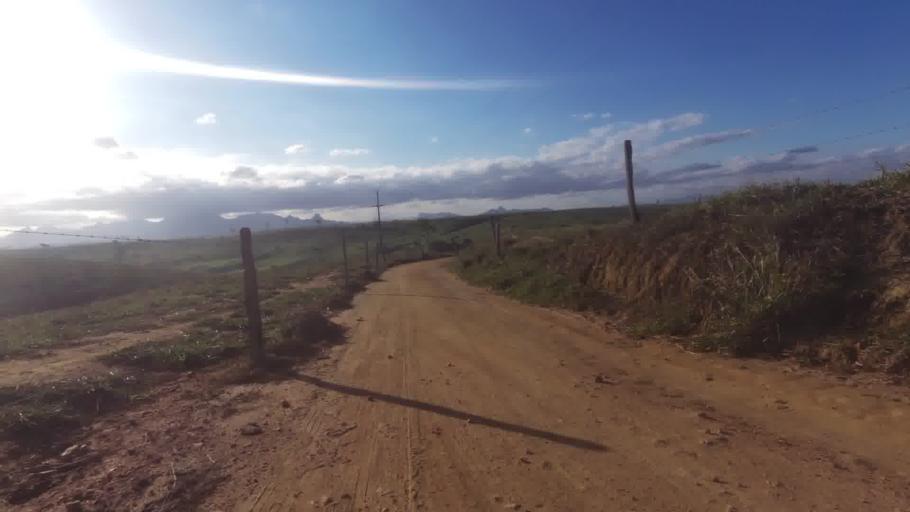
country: BR
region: Espirito Santo
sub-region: Marataizes
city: Marataizes
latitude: -21.1528
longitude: -41.0330
